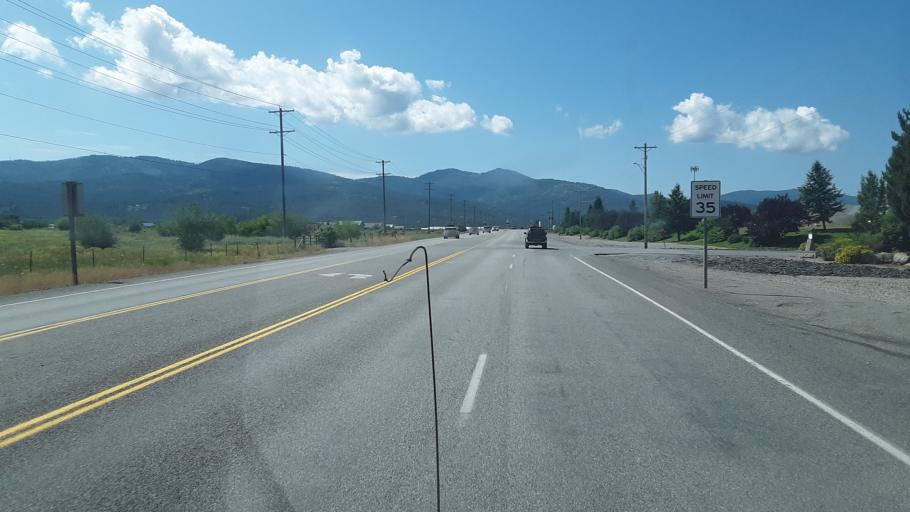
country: US
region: Idaho
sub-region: Kootenai County
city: Post Falls
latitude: 47.7224
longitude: -117.0019
